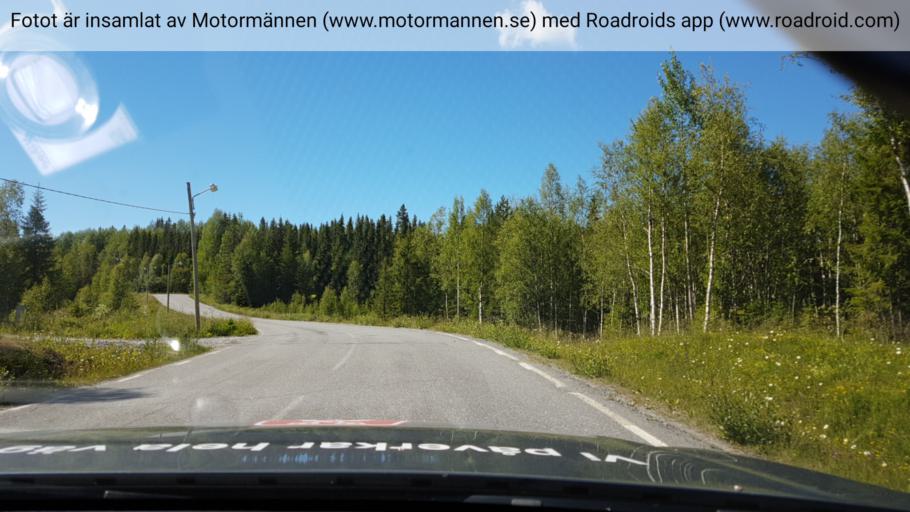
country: SE
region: Jaemtland
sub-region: Are Kommun
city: Are
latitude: 63.3108
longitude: 13.2213
